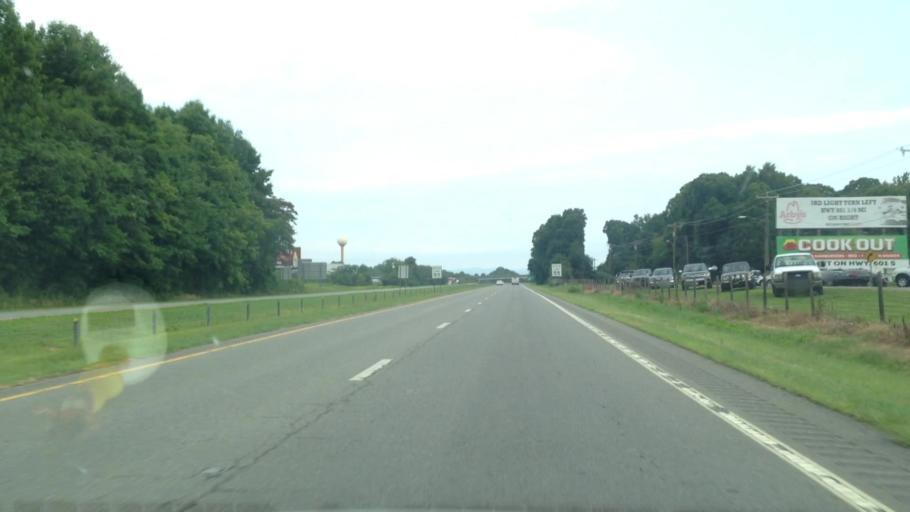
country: US
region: North Carolina
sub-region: Surry County
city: Flat Rock
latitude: 36.4552
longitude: -80.5555
